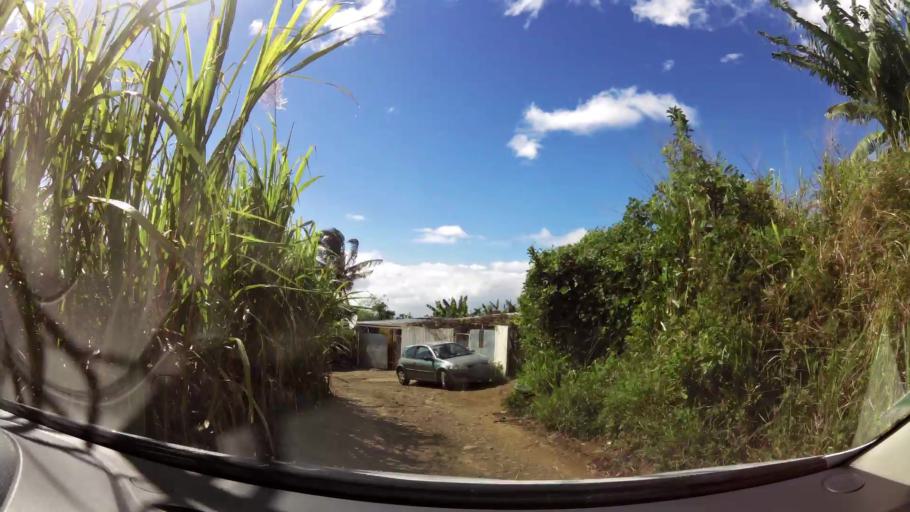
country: RE
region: Reunion
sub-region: Reunion
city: Sainte-Marie
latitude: -20.9265
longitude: 55.5051
